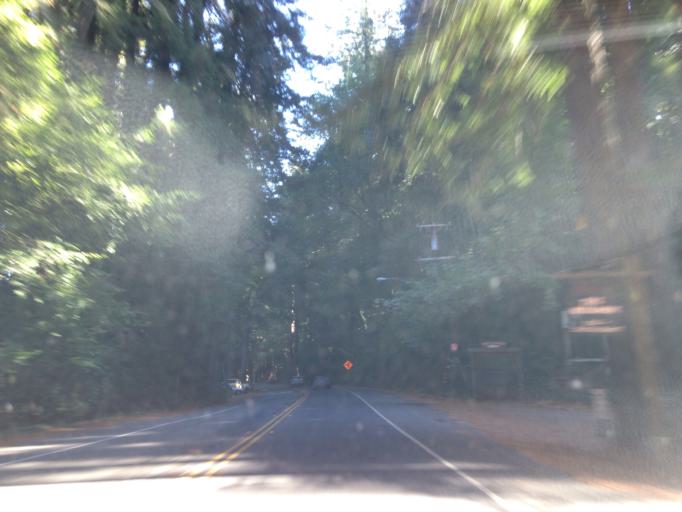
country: US
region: California
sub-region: Sonoma County
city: Monte Rio
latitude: 38.4856
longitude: -123.0147
